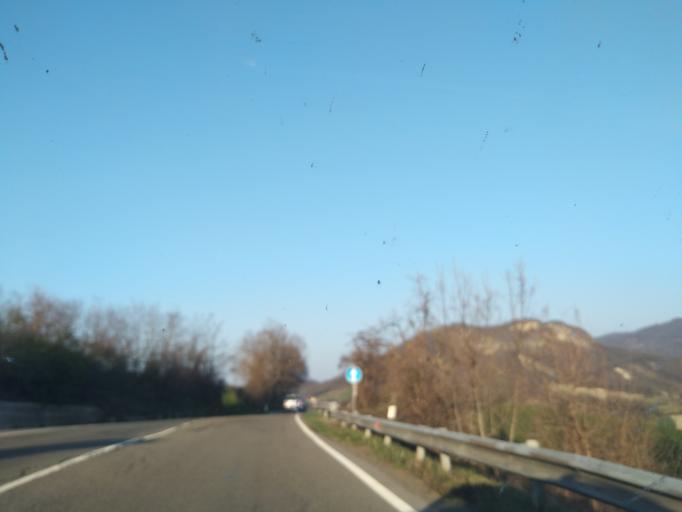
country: IT
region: Emilia-Romagna
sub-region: Provincia di Reggio Emilia
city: Felina
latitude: 44.4409
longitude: 10.4393
